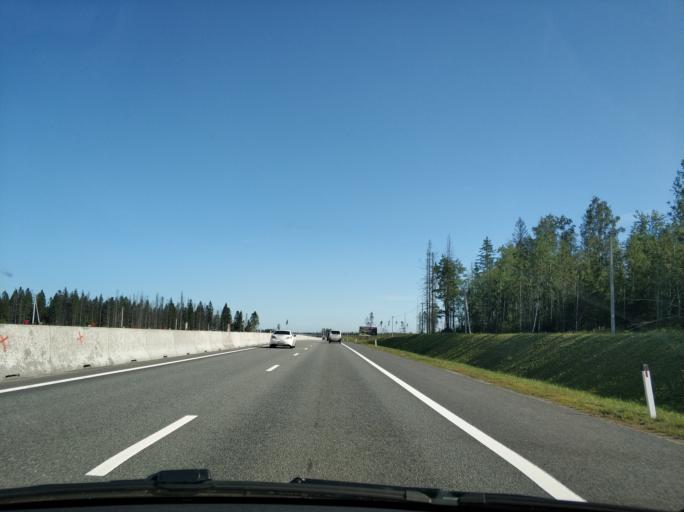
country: RU
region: Leningrad
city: Sosnovo
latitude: 60.4908
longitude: 30.1959
